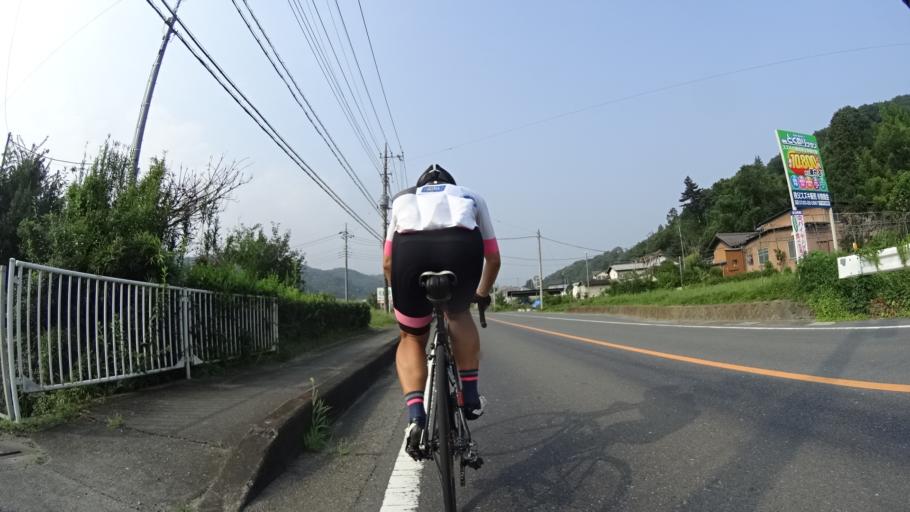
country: JP
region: Saitama
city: Chichibu
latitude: 36.0232
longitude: 139.0677
